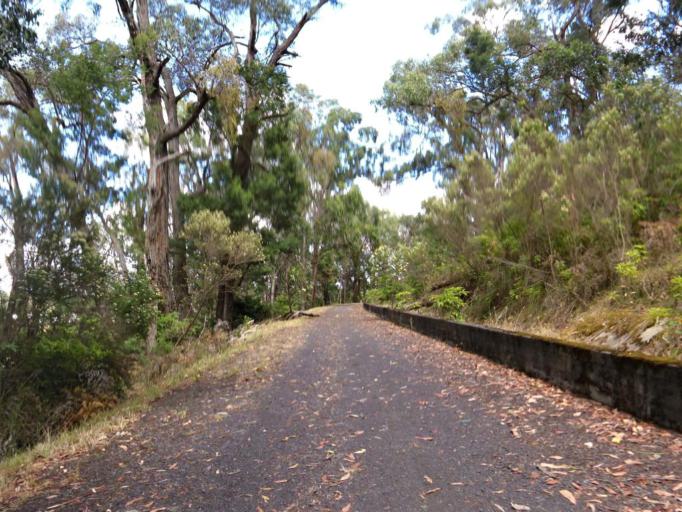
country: AU
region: Victoria
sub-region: Cardinia
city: Officer
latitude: -38.0350
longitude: 145.4382
